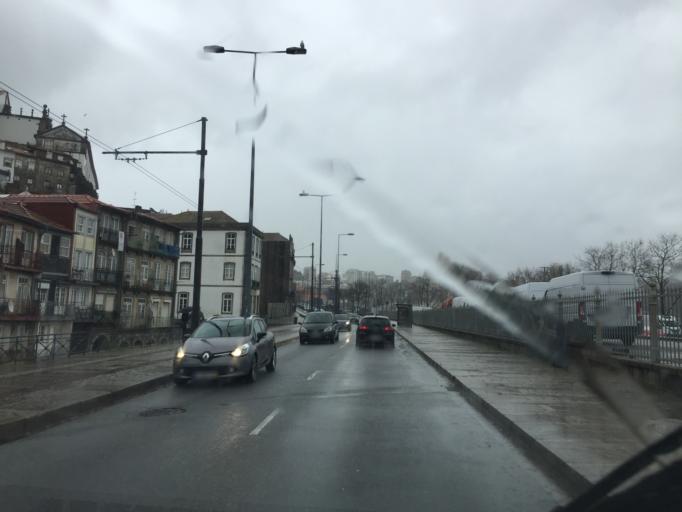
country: PT
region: Porto
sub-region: Vila Nova de Gaia
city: Vila Nova de Gaia
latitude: 41.1421
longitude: -8.6196
